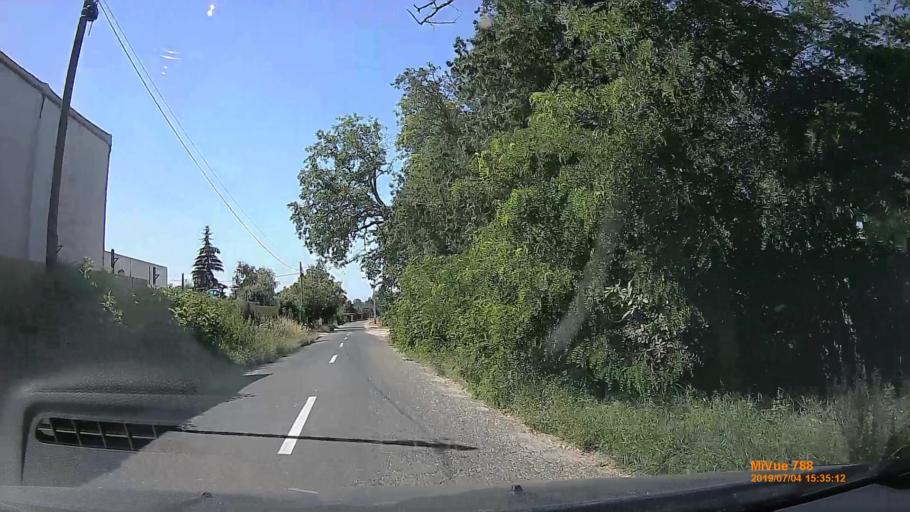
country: HU
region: Komarom-Esztergom
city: Tatabanya
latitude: 47.5402
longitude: 18.3857
